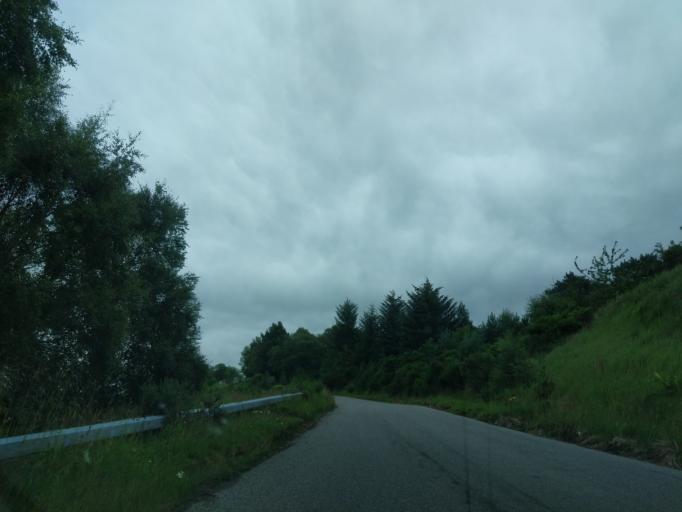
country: GB
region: Scotland
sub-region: Moray
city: Elgin
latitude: 57.5275
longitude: -3.4378
